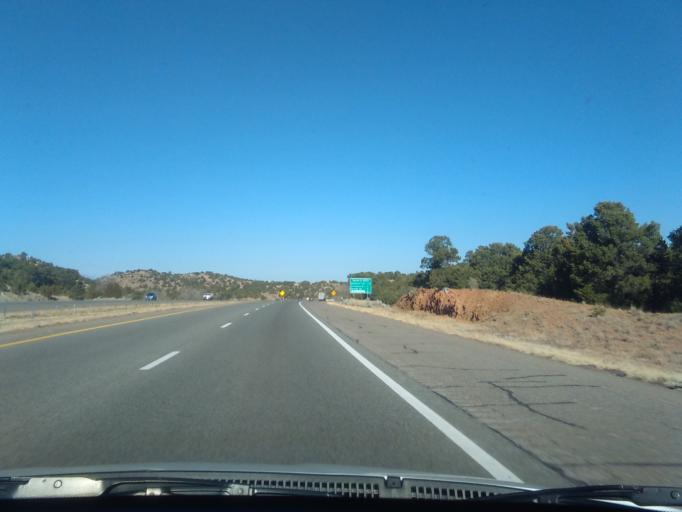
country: US
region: New Mexico
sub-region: Santa Fe County
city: Santa Fe
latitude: 35.6146
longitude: -105.9171
